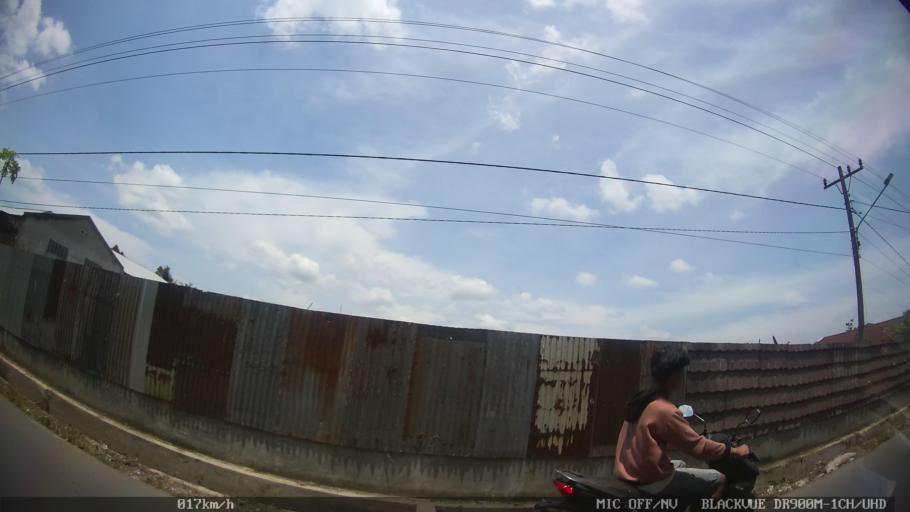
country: ID
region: North Sumatra
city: Sunggal
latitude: 3.5942
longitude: 98.5516
